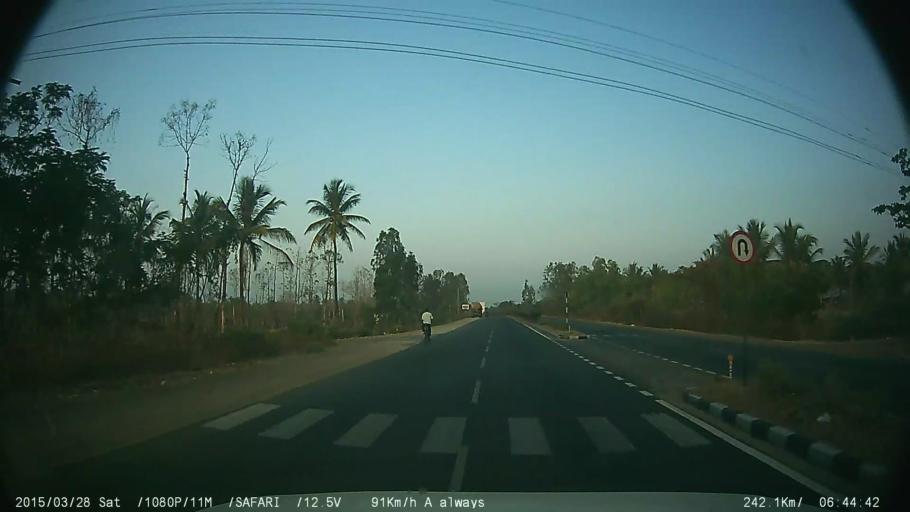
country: IN
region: Karnataka
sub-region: Mandya
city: Maddur
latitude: 12.6262
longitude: 77.1032
